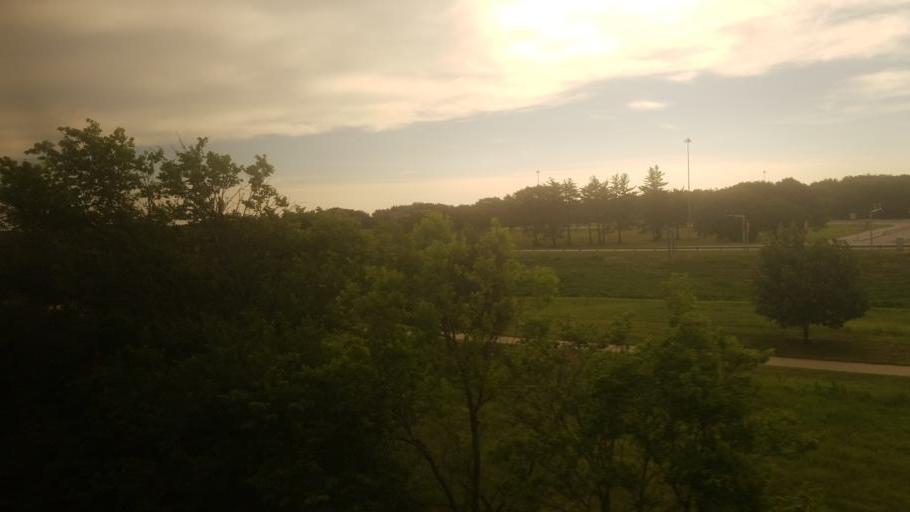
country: US
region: Kansas
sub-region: Shawnee County
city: Topeka
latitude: 39.0381
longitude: -95.6702
